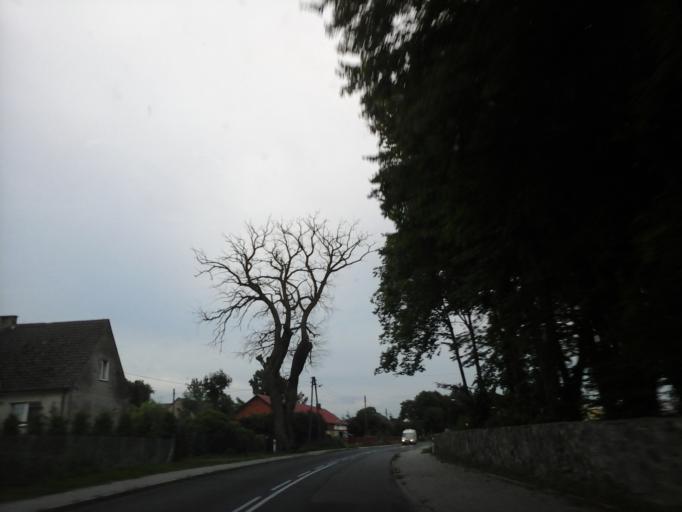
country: PL
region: West Pomeranian Voivodeship
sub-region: Powiat goleniowski
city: Maszewo
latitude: 53.4493
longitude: 15.0644
